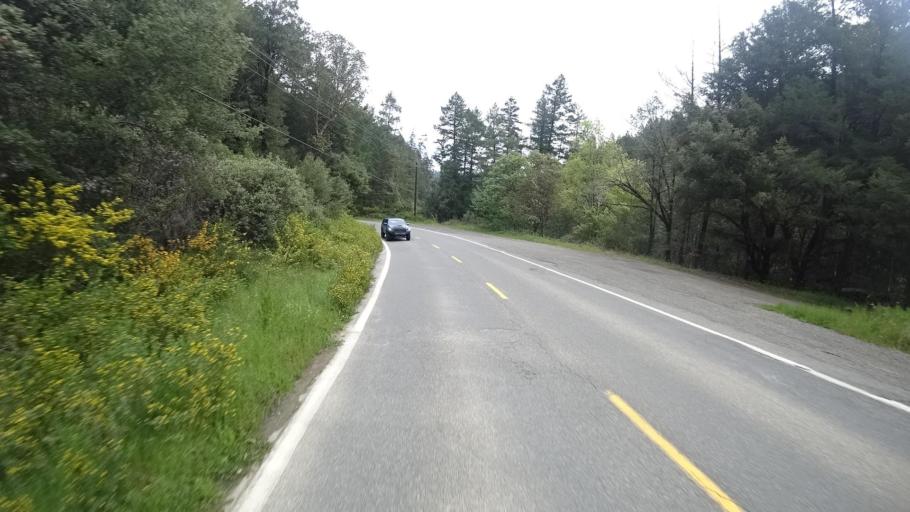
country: US
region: California
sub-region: Humboldt County
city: Redway
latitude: 40.1149
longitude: -123.8866
